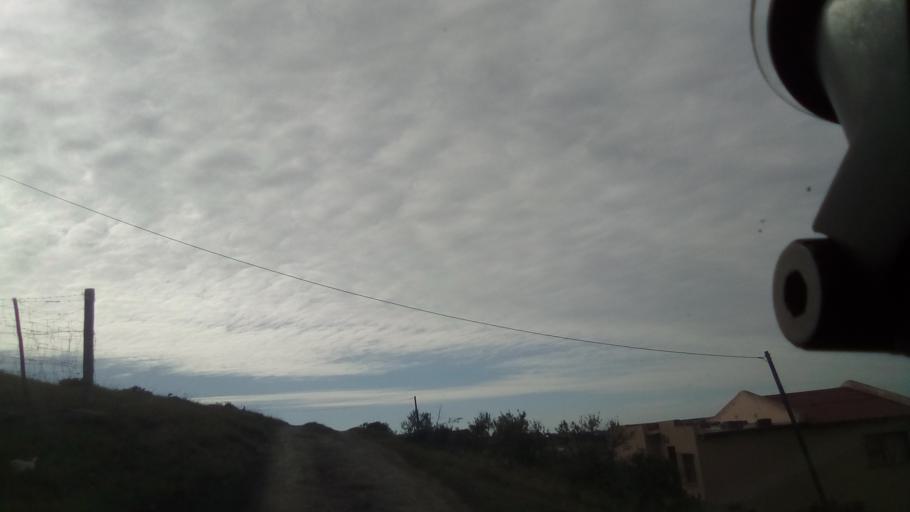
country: ZA
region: Eastern Cape
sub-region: Buffalo City Metropolitan Municipality
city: East London
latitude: -32.7962
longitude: 27.9565
